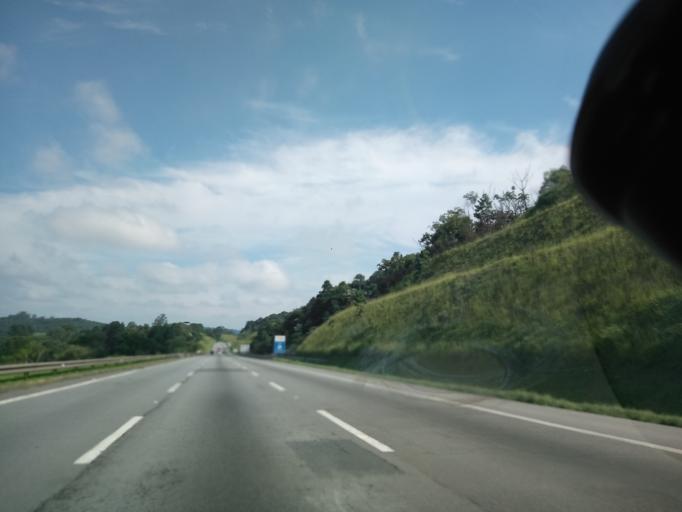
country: BR
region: Sao Paulo
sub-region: Embu
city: Embu
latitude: -23.6808
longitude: -46.8203
